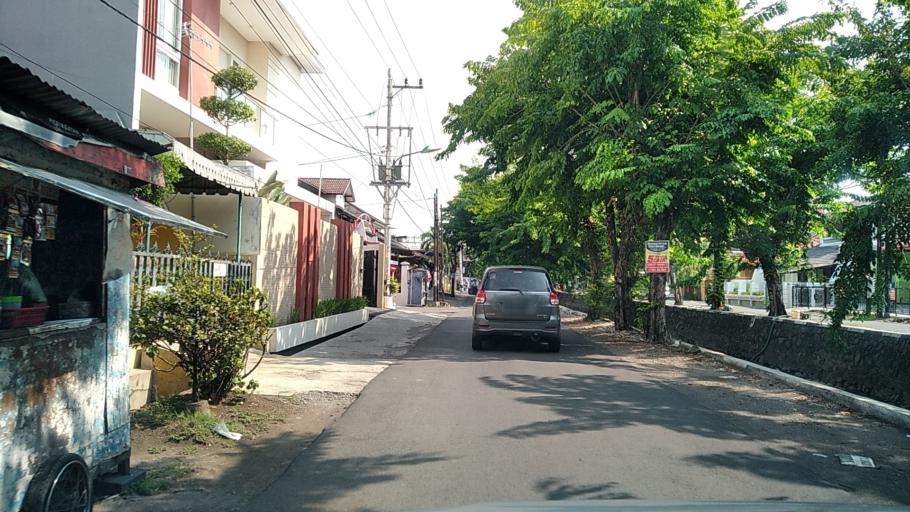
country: ID
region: Central Java
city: Semarang
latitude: -6.9864
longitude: 110.4373
